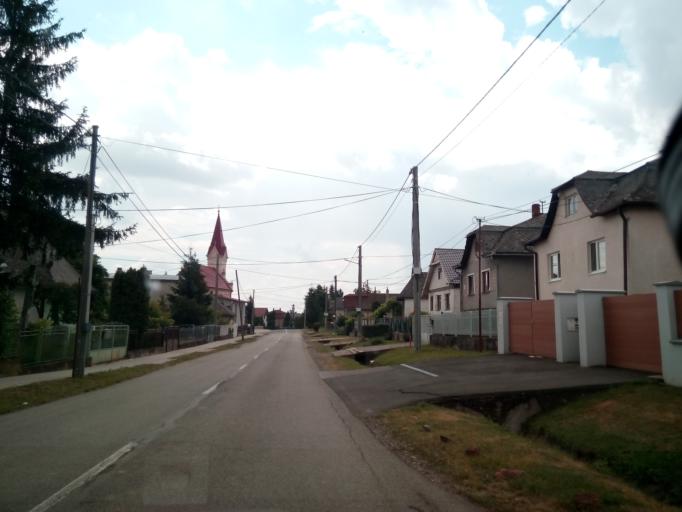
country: SK
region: Kosicky
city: Secovce
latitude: 48.5834
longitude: 21.5682
